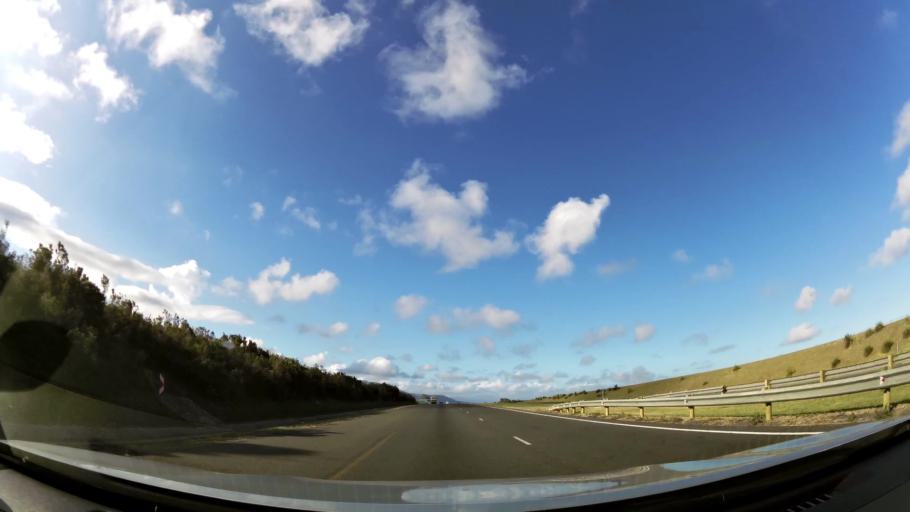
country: ZA
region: Western Cape
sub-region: Eden District Municipality
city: George
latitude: -33.9901
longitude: 22.5008
